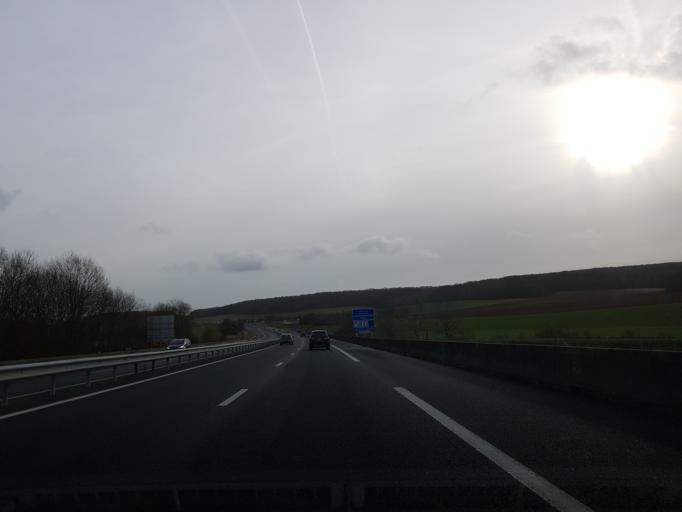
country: FR
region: Bourgogne
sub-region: Departement de l'Yonne
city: Soucy
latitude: 48.2503
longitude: 3.3414
